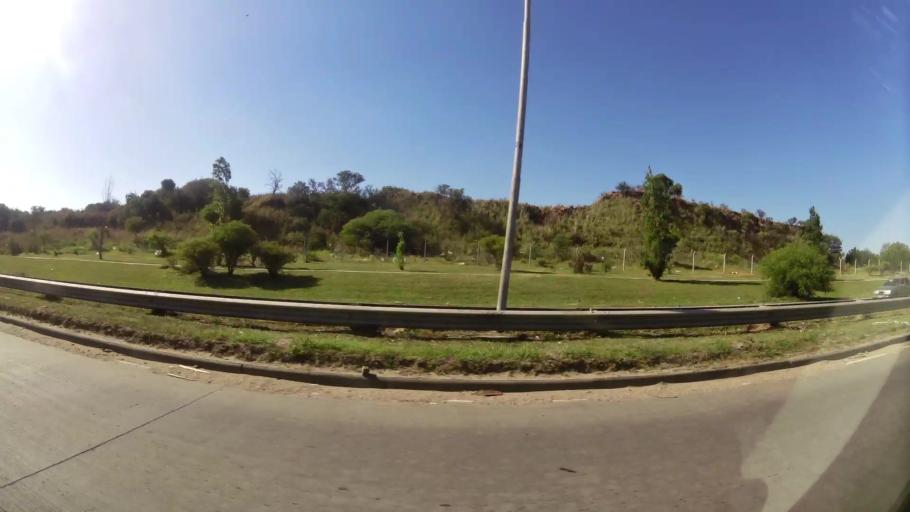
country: AR
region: Cordoba
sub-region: Departamento de Capital
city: Cordoba
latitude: -31.3981
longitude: -64.1327
